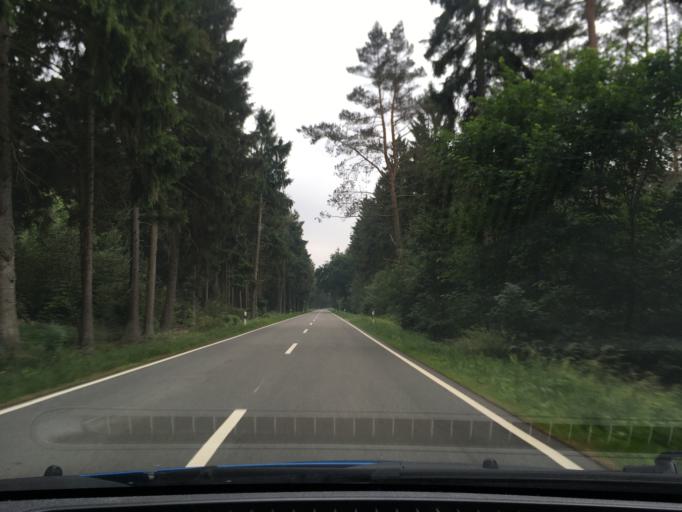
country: DE
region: Lower Saxony
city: Gohrde
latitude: 53.1264
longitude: 10.8643
